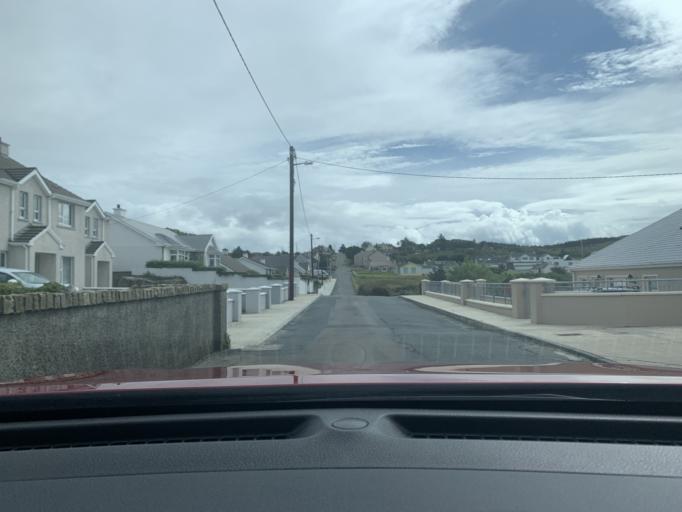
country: IE
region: Ulster
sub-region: County Donegal
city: Dungloe
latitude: 54.9474
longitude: -8.3594
